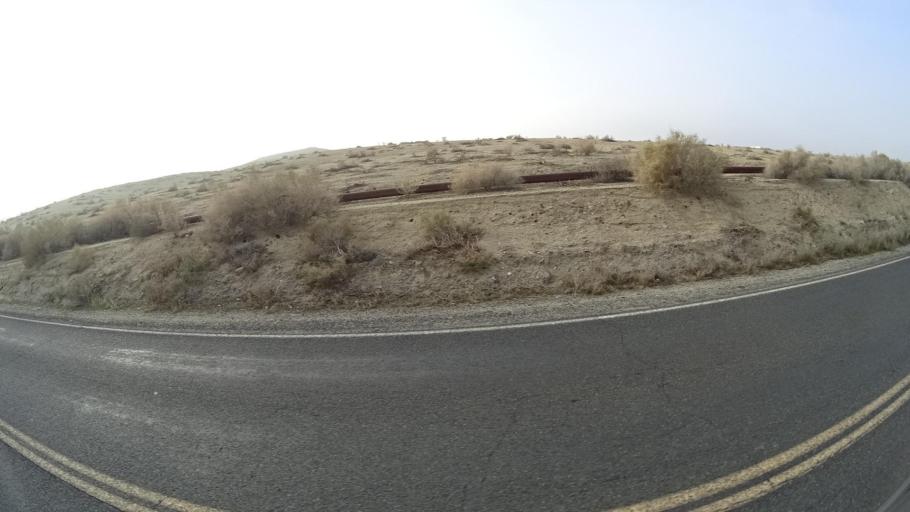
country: US
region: California
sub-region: Kern County
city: Ford City
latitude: 35.2054
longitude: -119.4456
